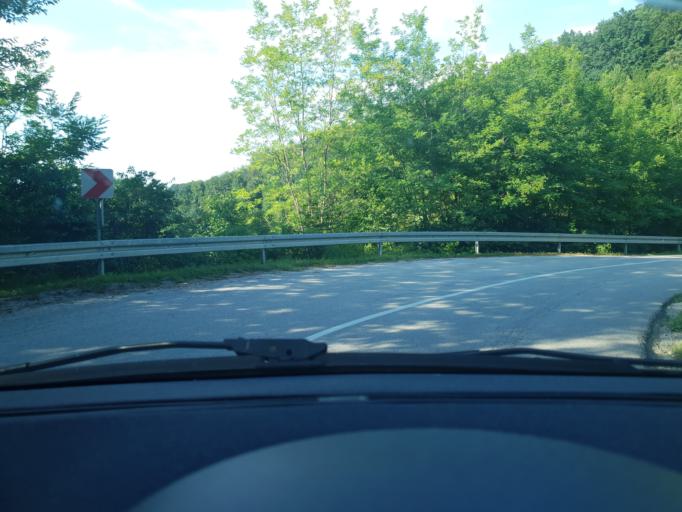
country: HR
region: Krapinsko-Zagorska
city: Pregrada
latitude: 46.0733
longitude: 15.7959
